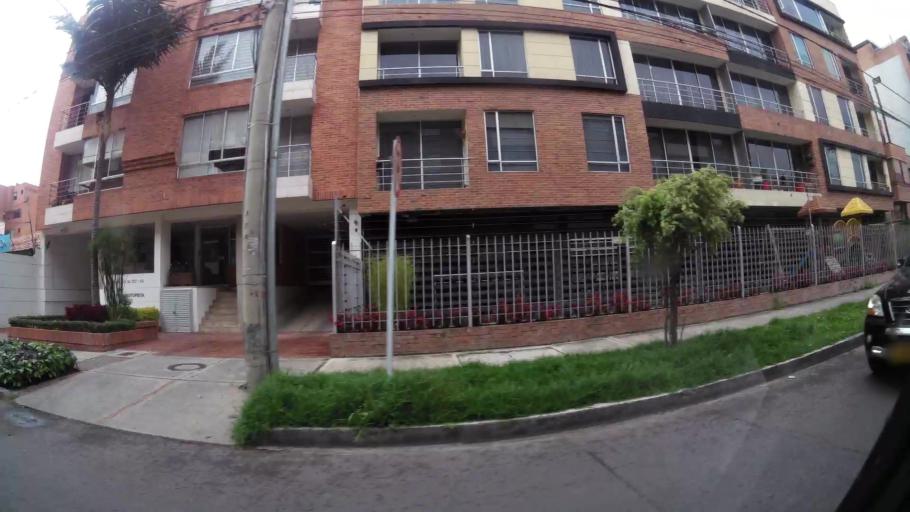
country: CO
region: Bogota D.C.
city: Barrio San Luis
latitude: 4.7225
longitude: -74.0481
